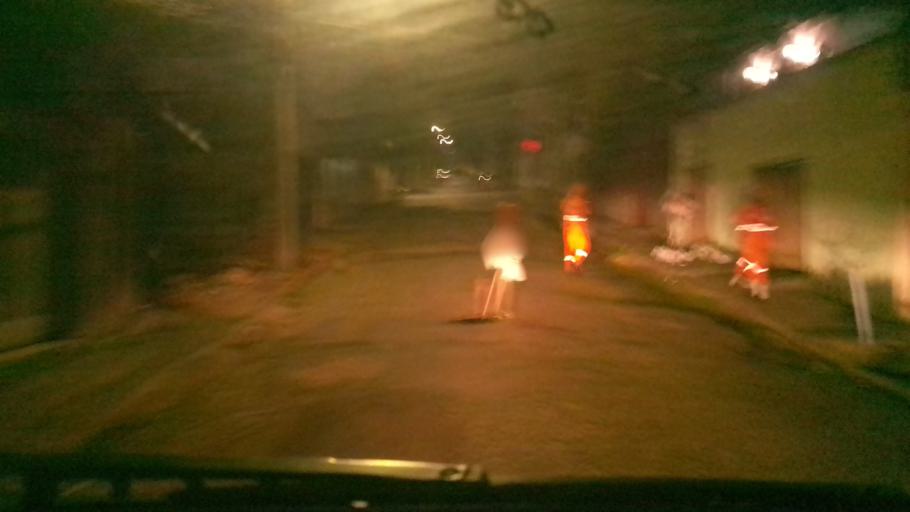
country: BR
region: Minas Gerais
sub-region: Belo Horizonte
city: Belo Horizonte
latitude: -19.9113
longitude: -43.9019
